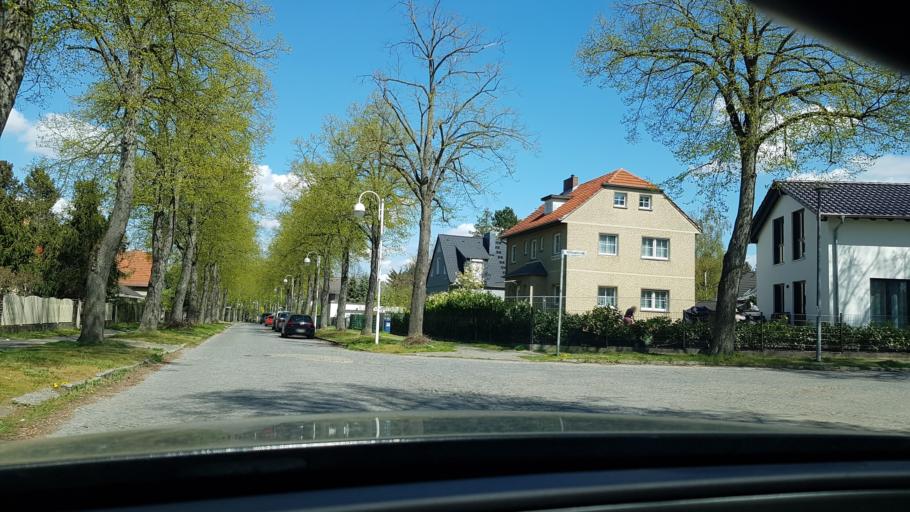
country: DE
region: Berlin
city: Lichtenrade
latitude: 52.3639
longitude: 13.4152
